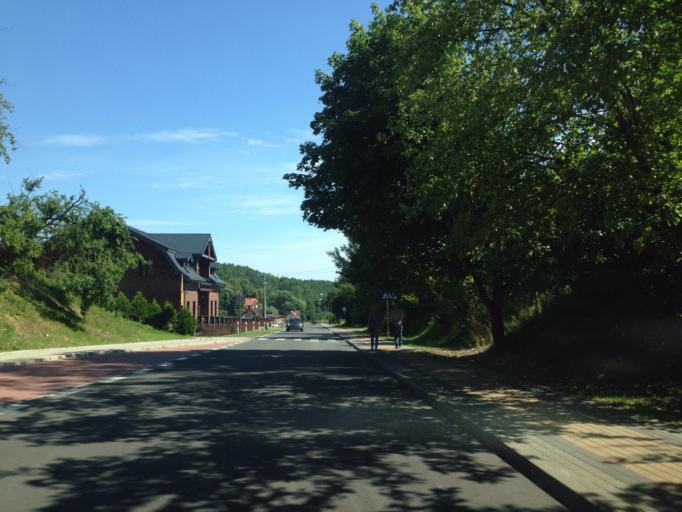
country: PL
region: Kujawsko-Pomorskie
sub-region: Powiat swiecki
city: Osie
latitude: 53.6199
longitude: 18.2661
